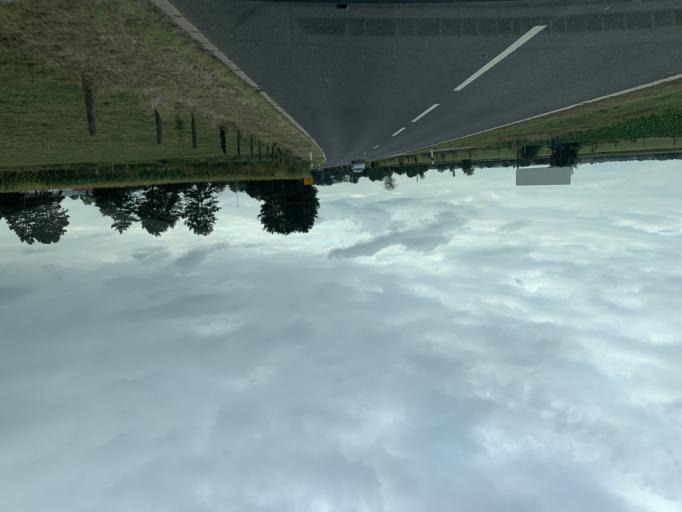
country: DE
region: North Rhine-Westphalia
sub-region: Regierungsbezirk Koln
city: Linnich
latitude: 51.0112
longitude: 6.2407
